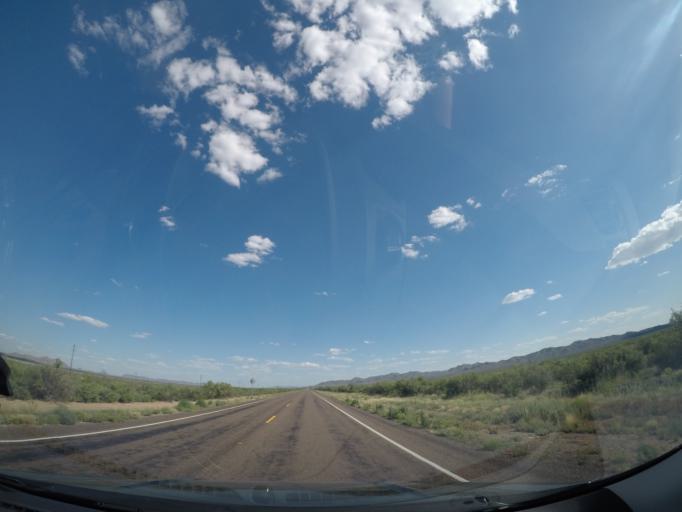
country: US
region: Texas
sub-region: Culberson County
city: Van Horn
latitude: 30.9766
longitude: -104.8190
